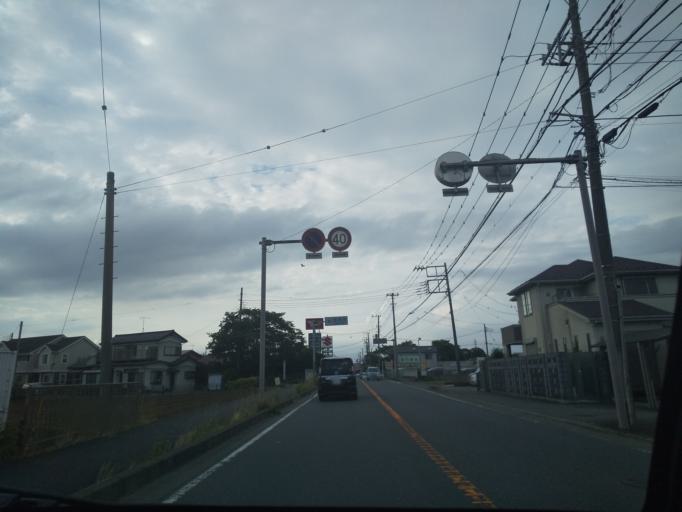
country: JP
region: Kanagawa
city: Zama
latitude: 35.4713
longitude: 139.3888
